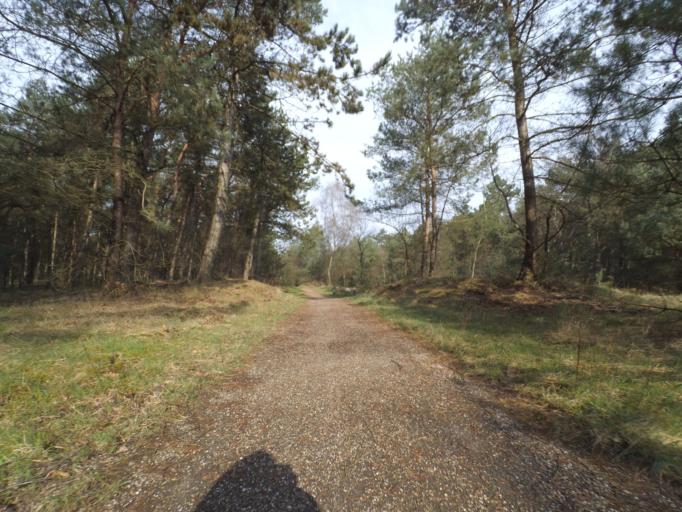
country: NL
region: Gelderland
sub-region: Gemeente Ede
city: Harskamp
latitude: 52.1576
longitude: 5.7350
